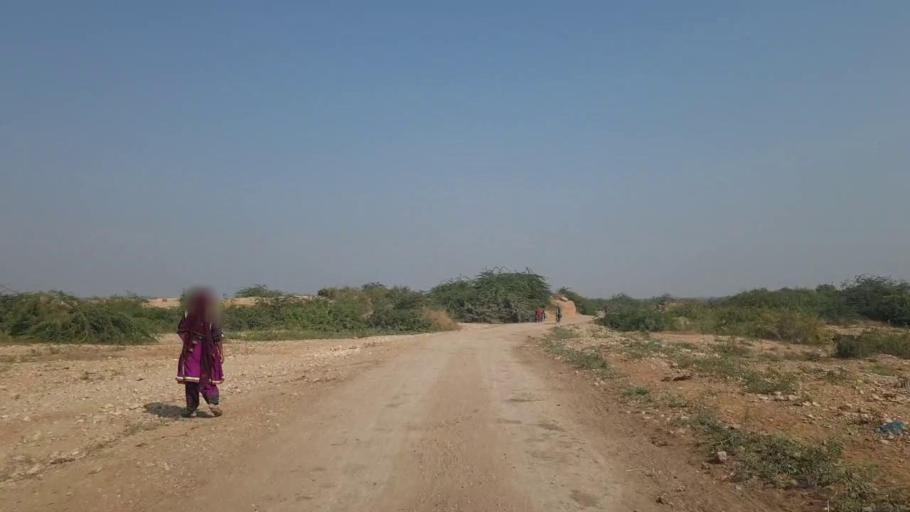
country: PK
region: Sindh
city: Matiari
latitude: 25.5453
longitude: 68.3524
